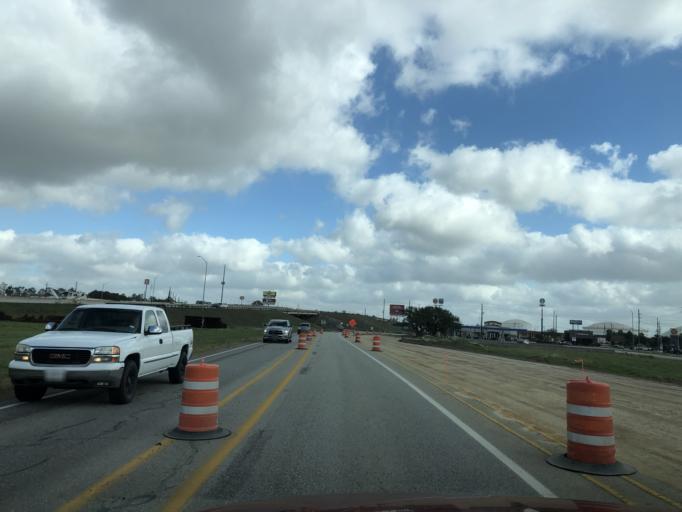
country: US
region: Texas
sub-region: Austin County
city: Sealy
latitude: 29.7629
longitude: -96.1549
